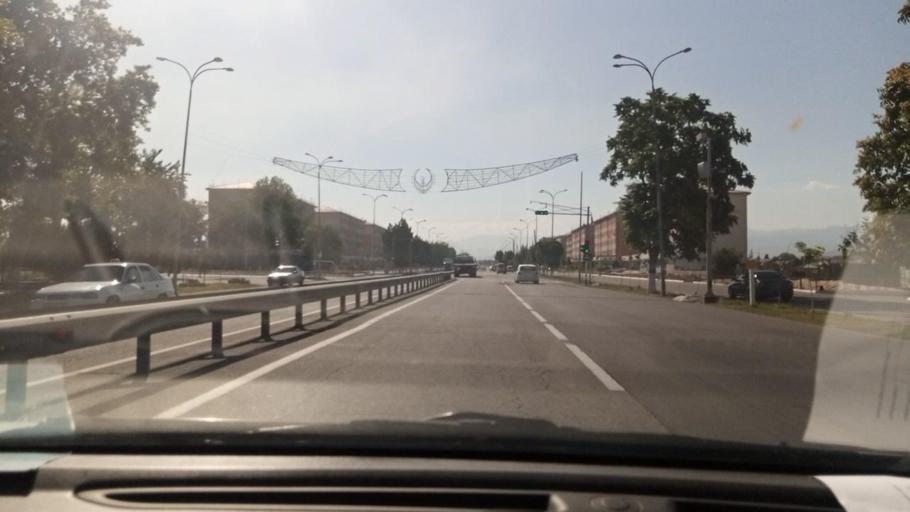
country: UZ
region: Toshkent
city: Ohangaron
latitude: 40.9095
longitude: 69.6240
